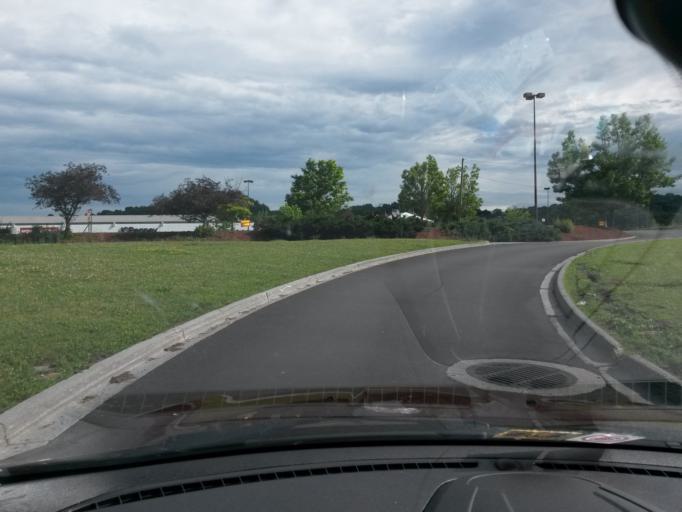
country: US
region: West Virginia
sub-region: Mercer County
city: Bluefield
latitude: 37.2945
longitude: -81.1661
